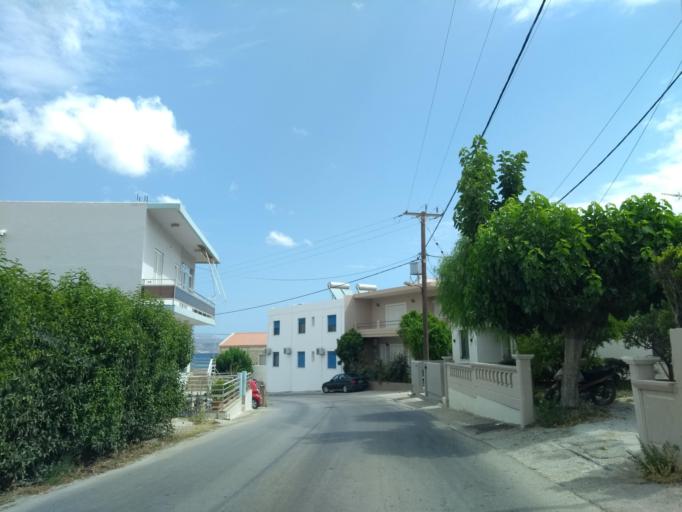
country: GR
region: Crete
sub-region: Nomos Chanias
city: Kalivai
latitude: 35.4502
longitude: 24.1758
